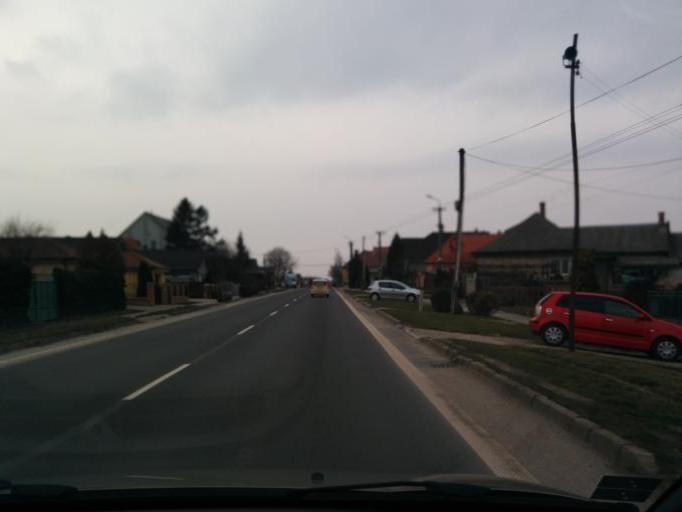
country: SK
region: Trnavsky
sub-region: Okres Galanta
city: Galanta
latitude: 48.2842
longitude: 17.7649
